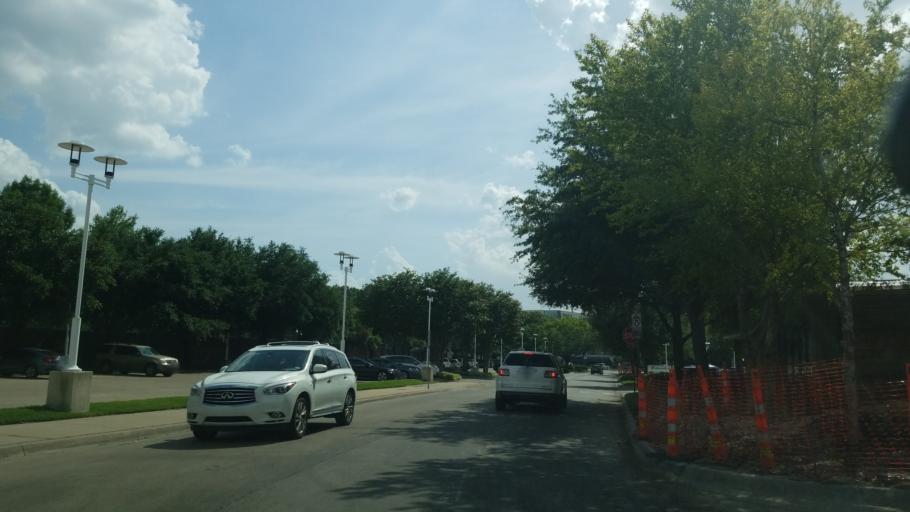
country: US
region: Texas
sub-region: Dallas County
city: University Park
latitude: 32.8632
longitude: -96.8023
